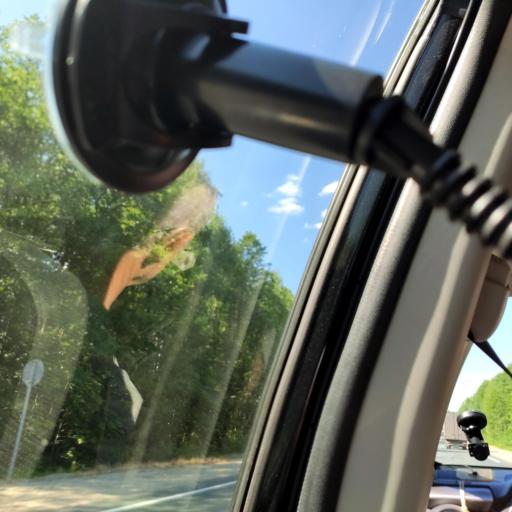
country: RU
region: Mariy-El
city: Suslonger
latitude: 56.2298
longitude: 48.2333
